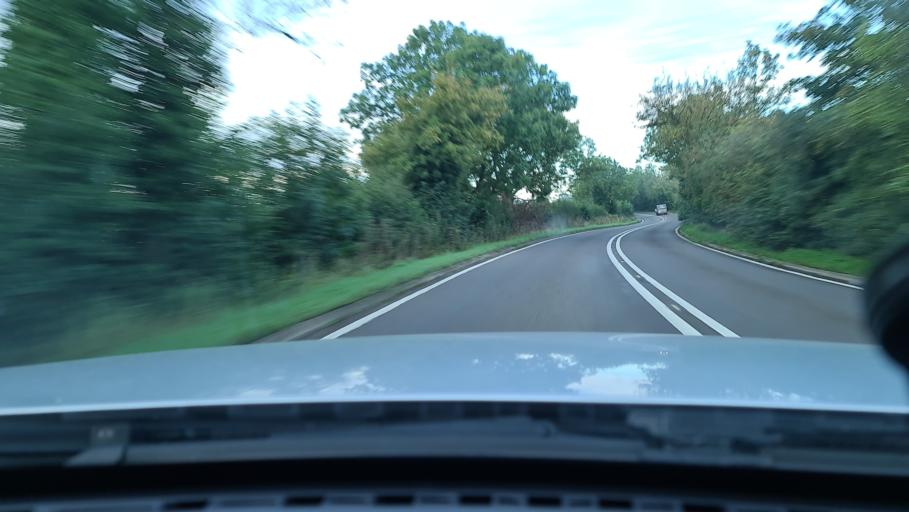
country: GB
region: England
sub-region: Oxfordshire
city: Claydon
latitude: 52.1549
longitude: -1.3625
